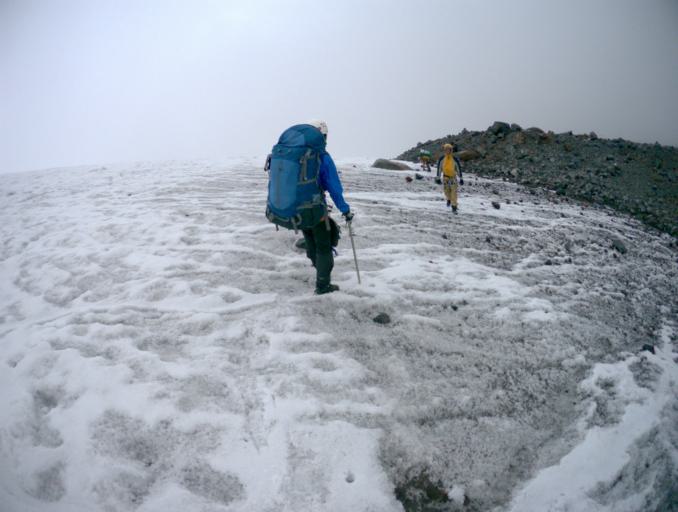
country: RU
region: Kabardino-Balkariya
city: Terskol
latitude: 43.3706
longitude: 42.4957
